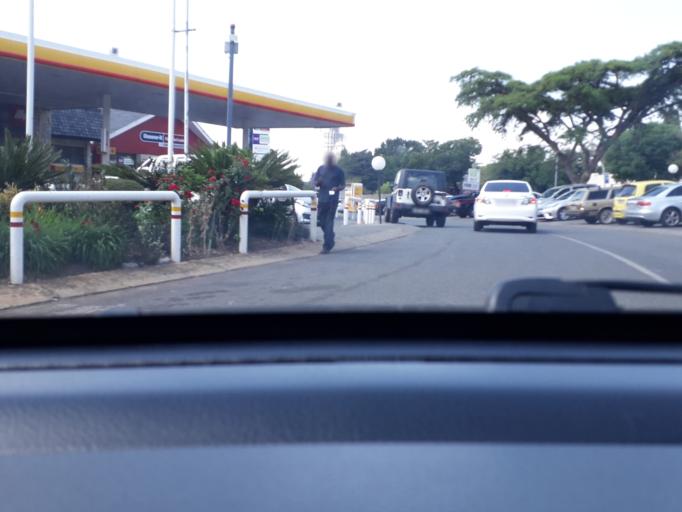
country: ZA
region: Gauteng
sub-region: City of Johannesburg Metropolitan Municipality
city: Johannesburg
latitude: -26.1169
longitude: 28.0458
